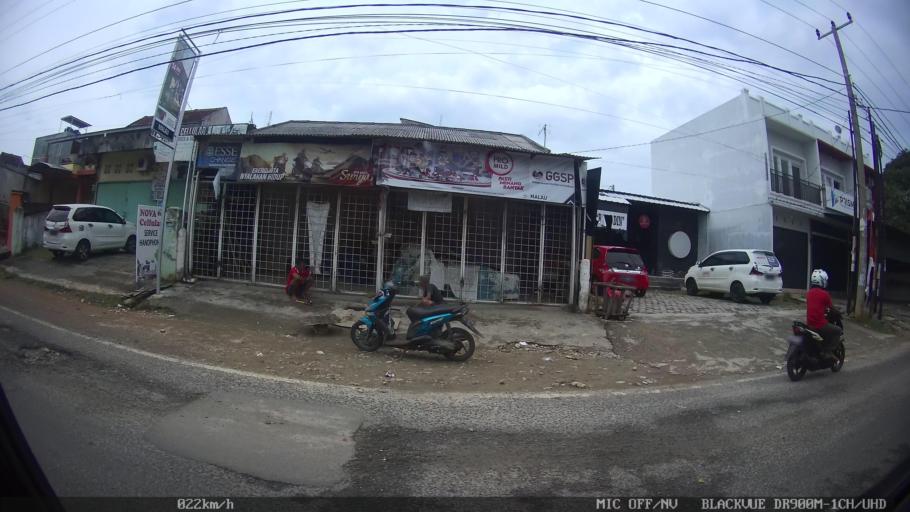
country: ID
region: Lampung
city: Kedaton
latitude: -5.3758
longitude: 105.2173
